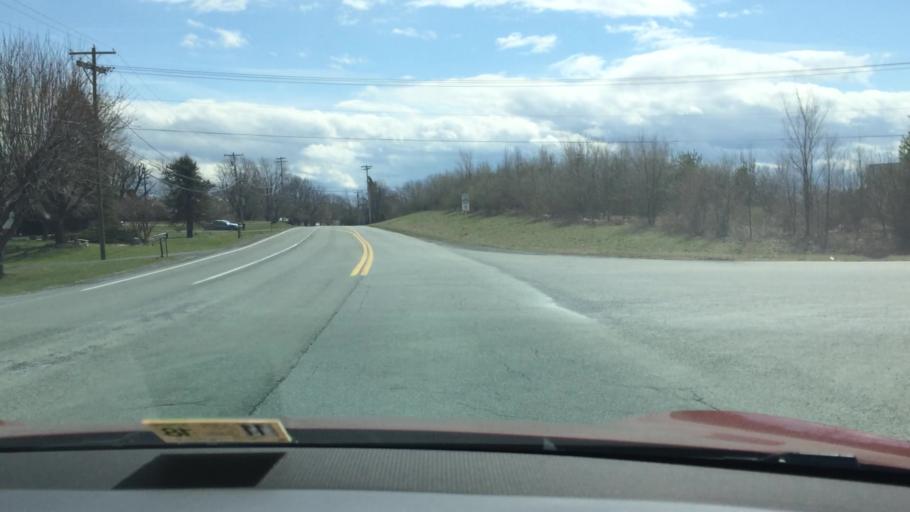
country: US
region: Virginia
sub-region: City of Winchester
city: Winchester
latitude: 39.2296
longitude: -78.1399
